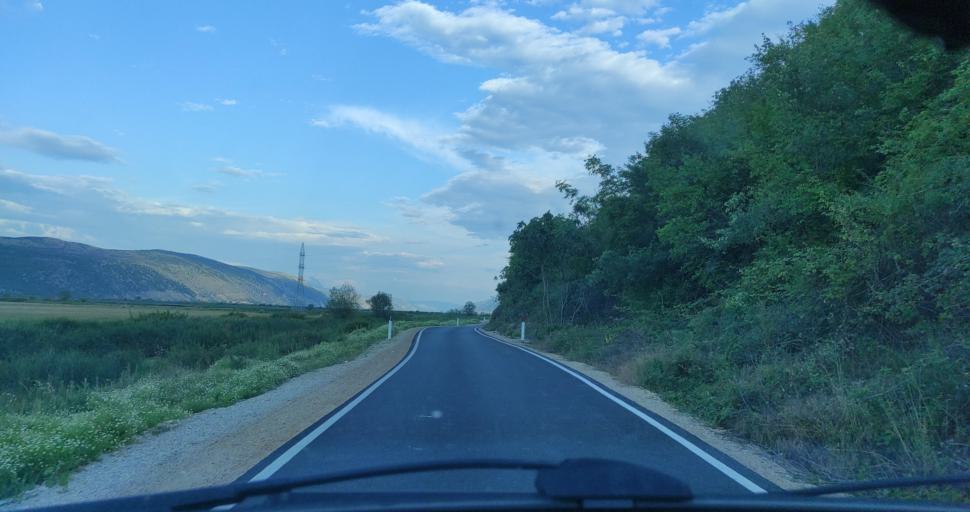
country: AL
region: Shkoder
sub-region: Rrethi i Shkodres
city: Velipoje
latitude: 41.9286
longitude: 19.4453
